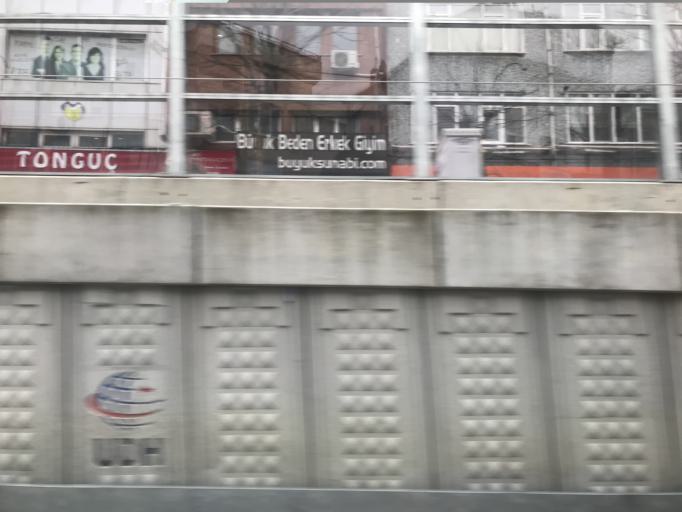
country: TR
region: Istanbul
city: Bahcelievler
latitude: 40.9809
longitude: 28.8761
